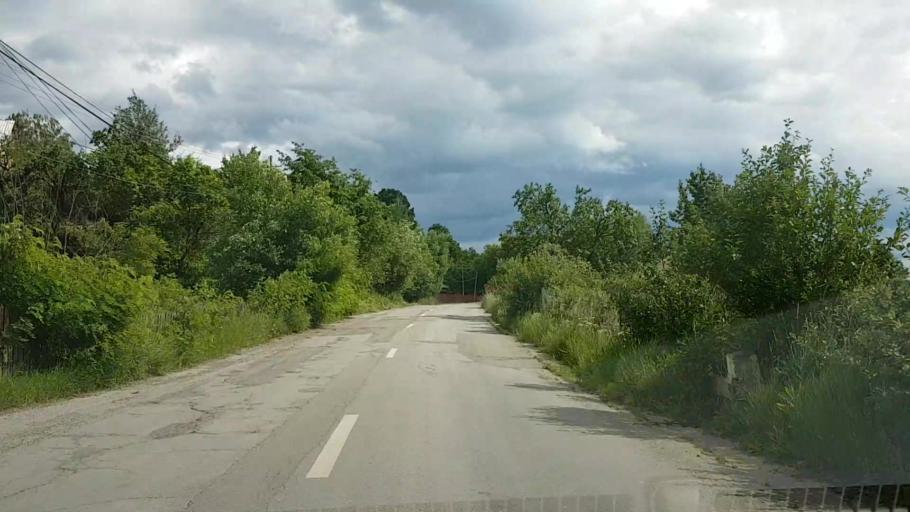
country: RO
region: Neamt
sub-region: Comuna Hangu
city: Hangu
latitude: 47.0420
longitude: 26.0558
